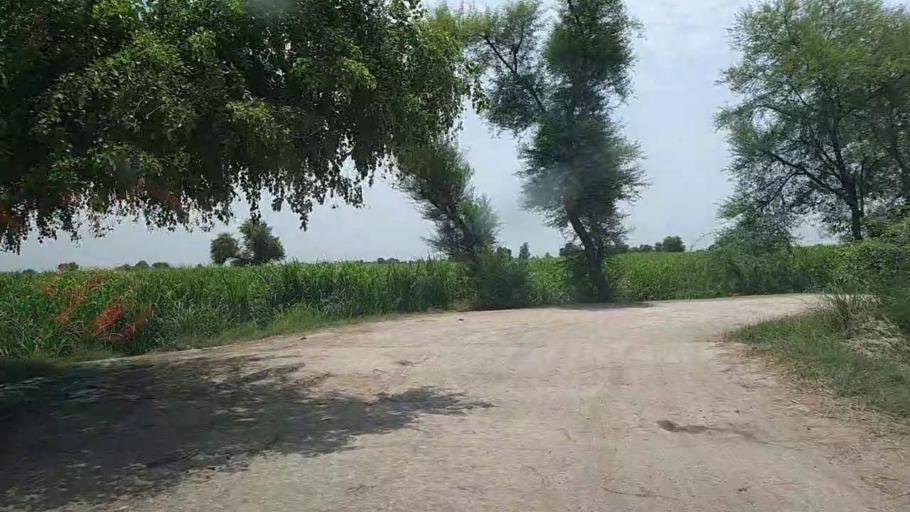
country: PK
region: Sindh
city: Pano Aqil
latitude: 27.8319
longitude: 69.1875
